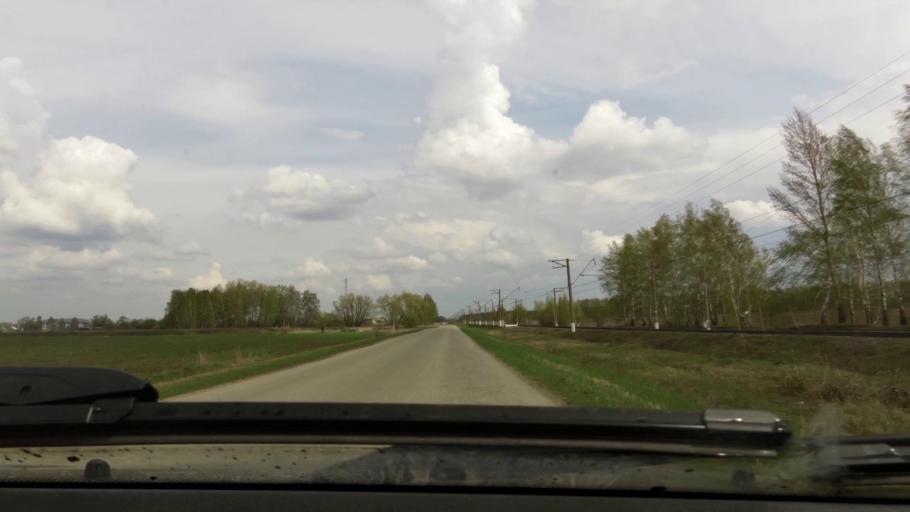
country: RU
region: Rjazan
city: Bagramovo
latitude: 54.7149
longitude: 39.3591
